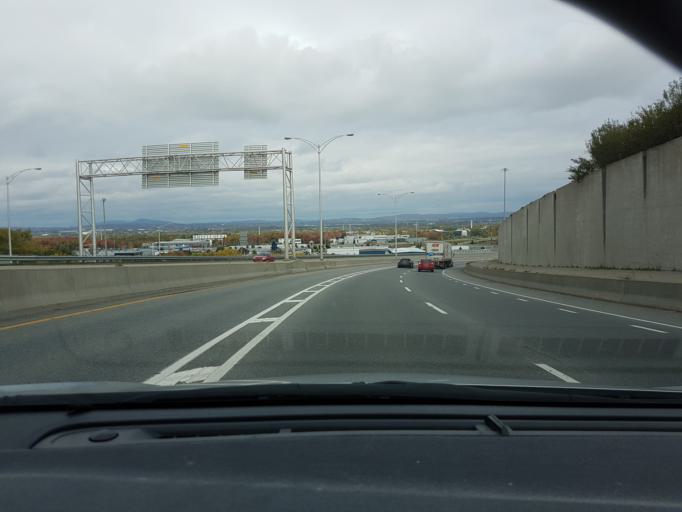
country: CA
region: Quebec
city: L'Ancienne-Lorette
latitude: 46.7876
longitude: -71.2909
